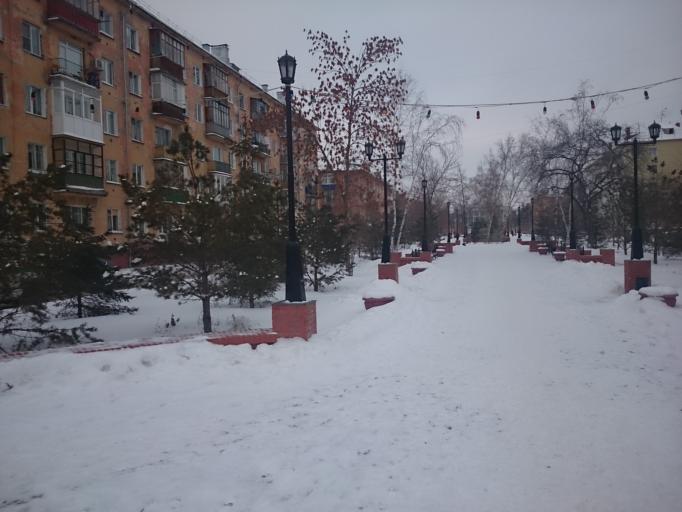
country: RU
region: Omsk
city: Omsk
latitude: 55.0264
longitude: 73.2780
